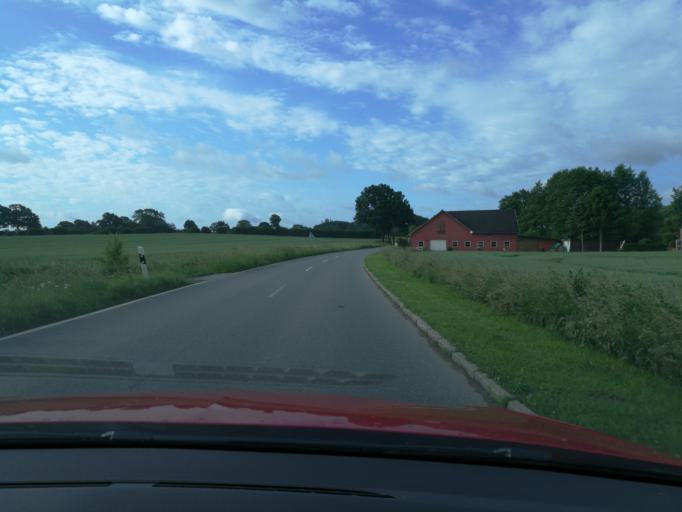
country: DE
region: Schleswig-Holstein
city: Todendorf
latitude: 53.6831
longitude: 10.3401
